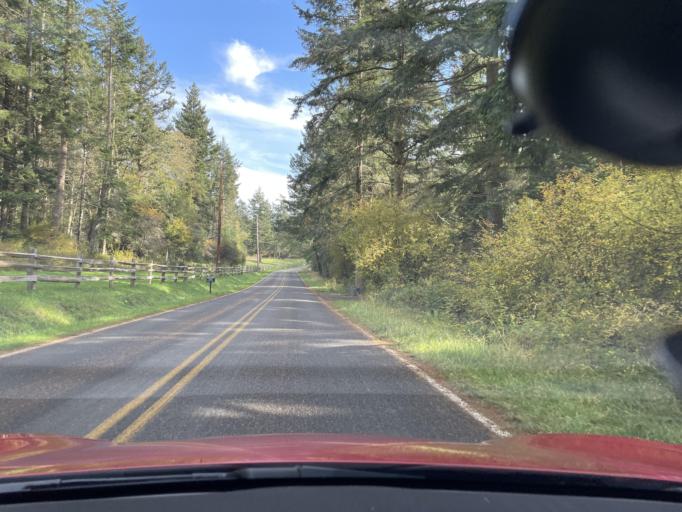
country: US
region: Washington
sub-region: San Juan County
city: Friday Harbor
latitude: 48.5186
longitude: -122.9908
